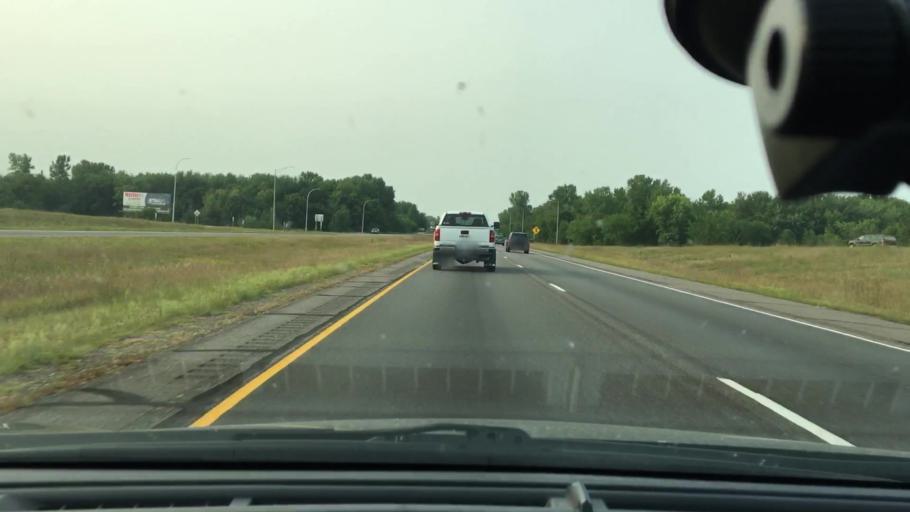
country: US
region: Minnesota
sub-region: Mille Lacs County
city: Princeton
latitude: 45.5788
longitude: -93.5997
